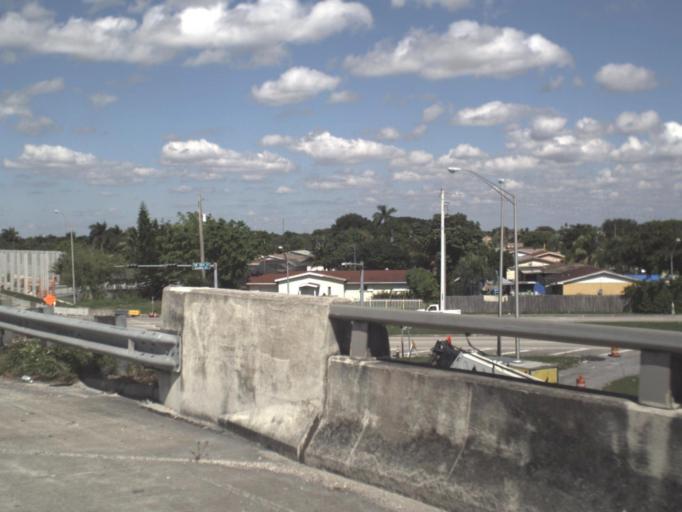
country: US
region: Florida
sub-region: Miami-Dade County
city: South Miami Heights
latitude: 25.5971
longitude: -80.3739
